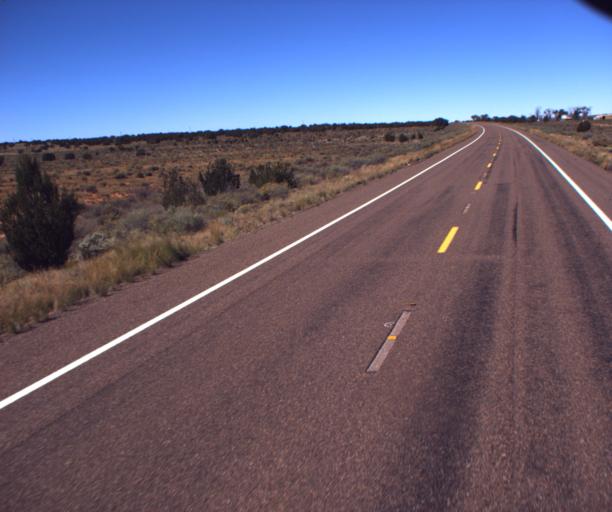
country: US
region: Arizona
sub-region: Apache County
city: Saint Johns
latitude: 34.6123
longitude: -109.6516
